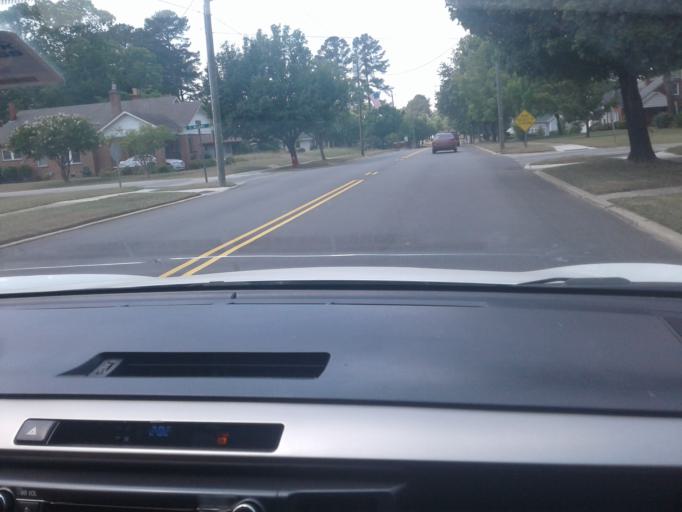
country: US
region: North Carolina
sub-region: Johnston County
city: Benson
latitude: 35.3844
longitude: -78.5531
